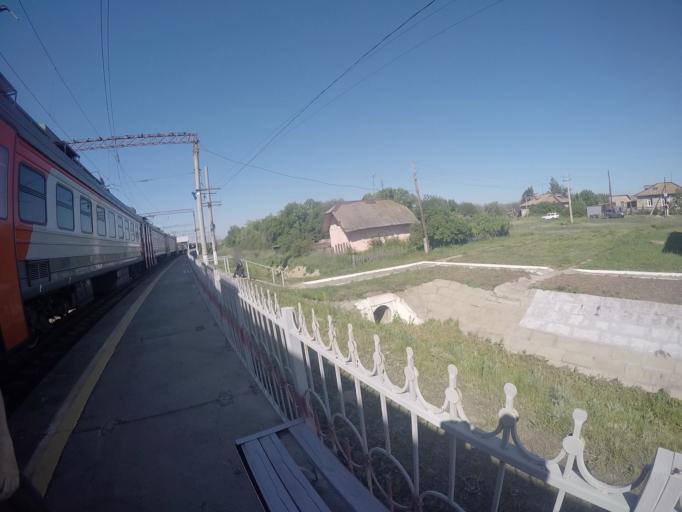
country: RU
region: Saratov
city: Krasnoarmeysk
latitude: 51.2576
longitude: 45.5924
